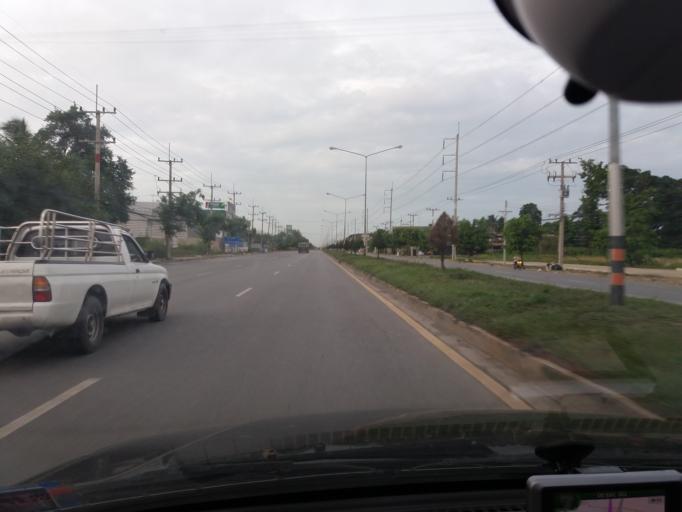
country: TH
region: Suphan Buri
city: U Thong
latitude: 14.3966
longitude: 99.8958
